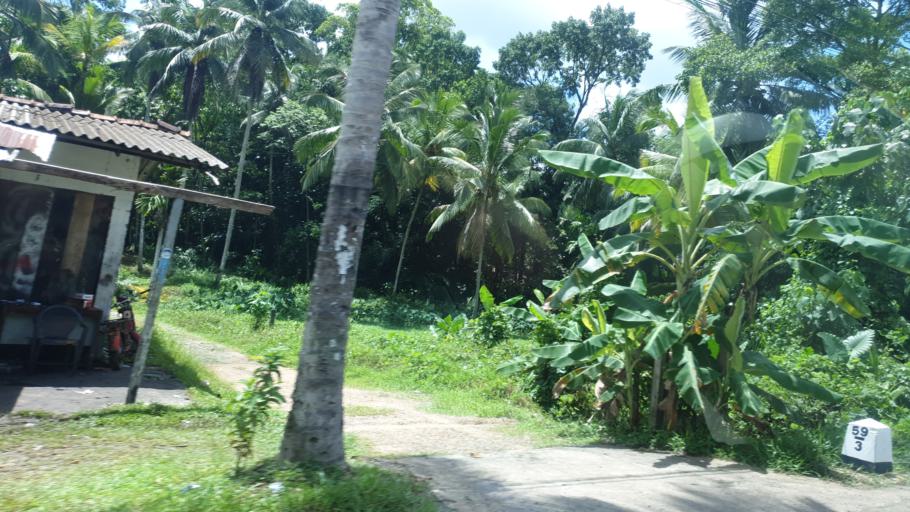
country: LK
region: Western
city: Horawala Junction
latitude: 6.5231
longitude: 80.2170
